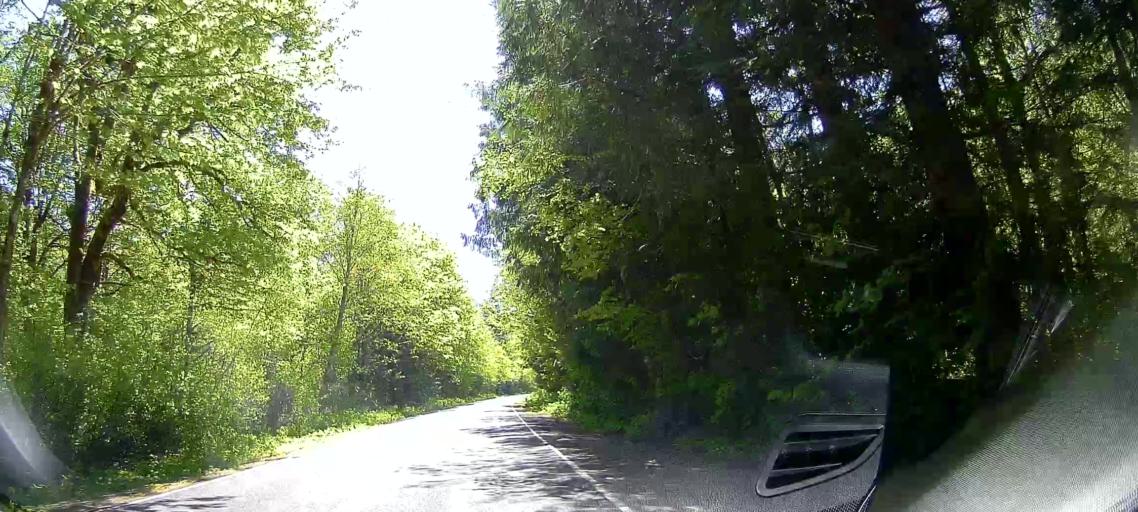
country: US
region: Washington
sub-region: Snohomish County
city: Darrington
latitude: 48.4323
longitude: -121.5744
